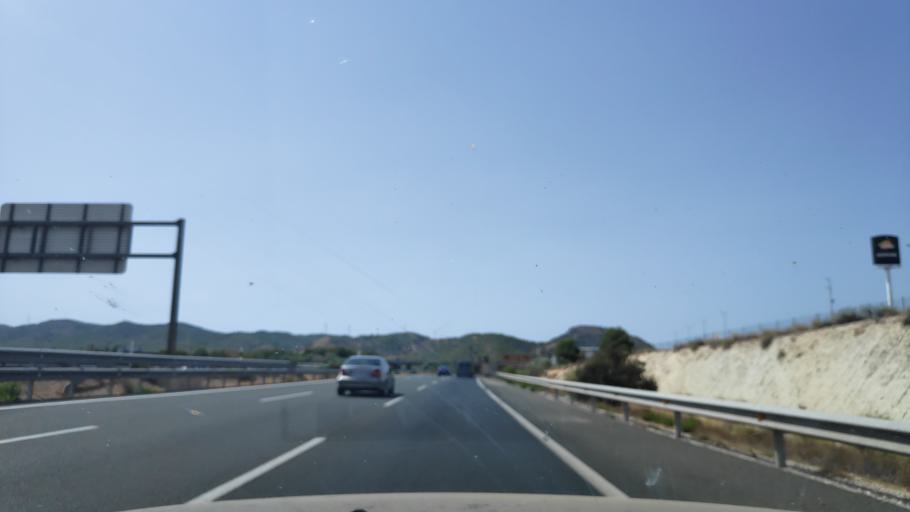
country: ES
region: Murcia
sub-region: Murcia
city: Murcia
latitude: 37.8834
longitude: -1.1358
